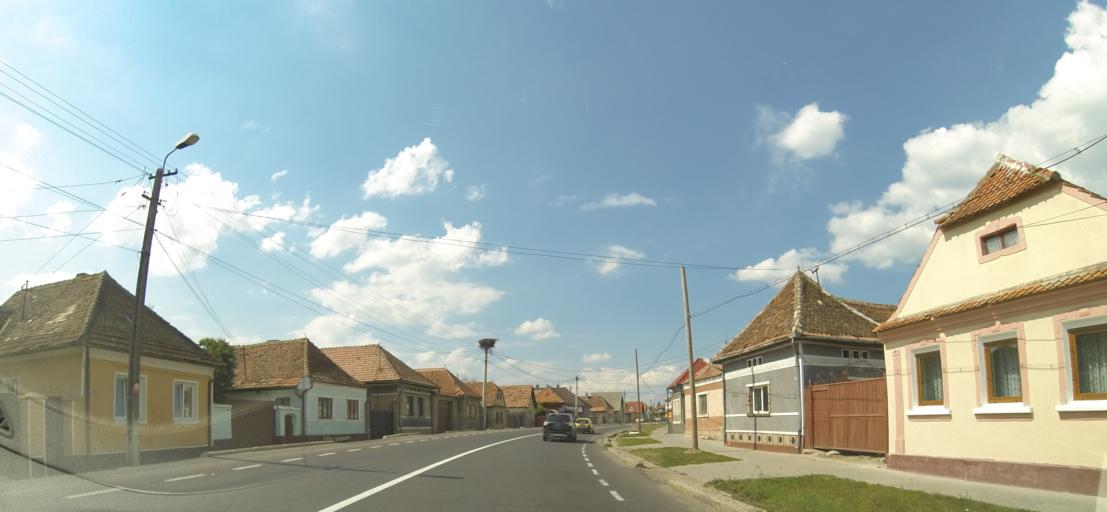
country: RO
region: Brasov
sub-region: Comuna Dumbravita
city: Dumbravita
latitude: 45.7652
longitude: 25.3710
